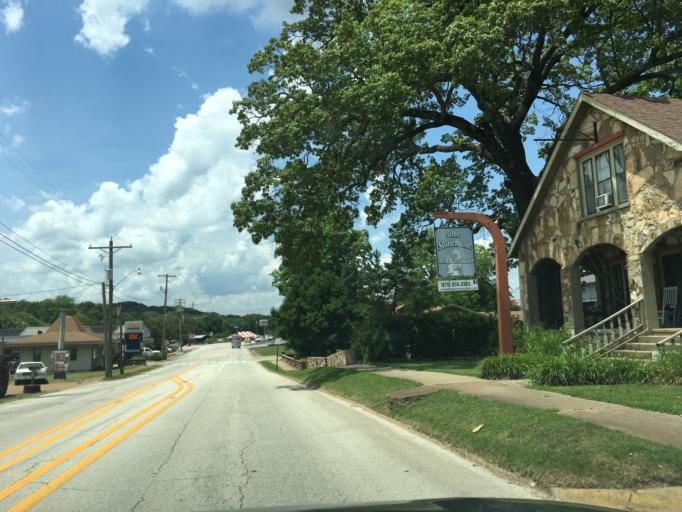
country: US
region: Arkansas
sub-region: Sharp County
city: Cherokee Village
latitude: 36.3156
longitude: -91.4832
